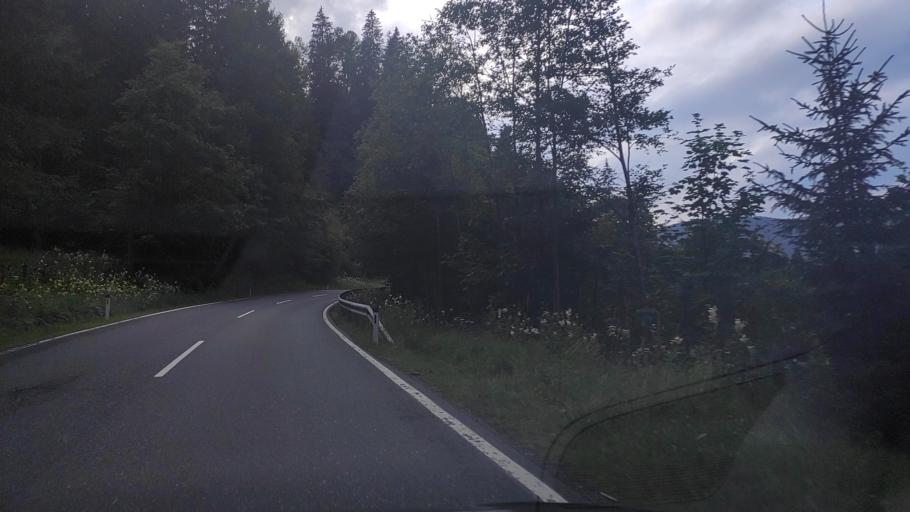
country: AT
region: Salzburg
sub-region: Politischer Bezirk Zell am See
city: Taxenbach
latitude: 47.2691
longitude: 12.9780
